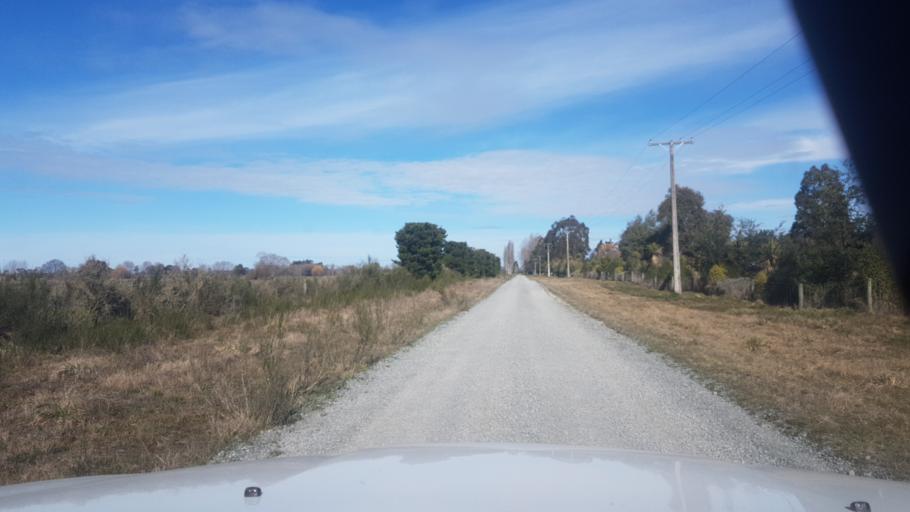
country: NZ
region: Canterbury
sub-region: Timaru District
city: Pleasant Point
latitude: -44.1449
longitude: 171.2814
